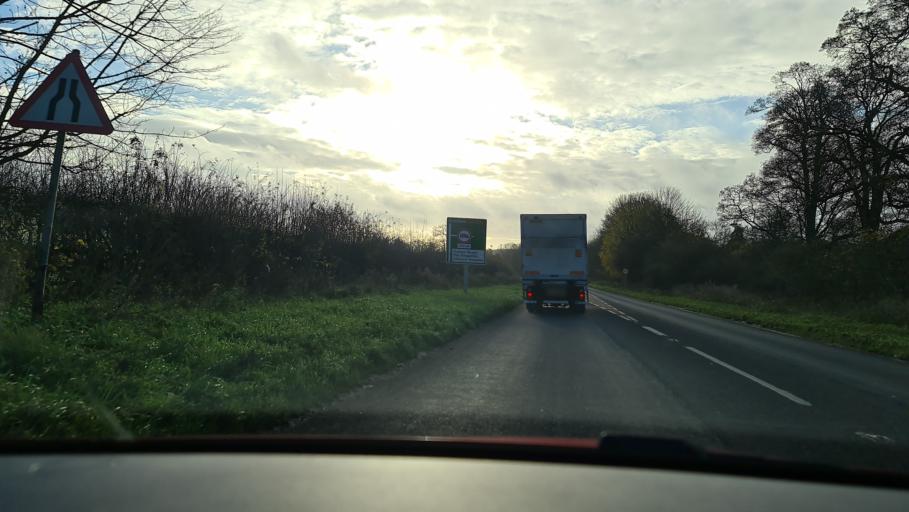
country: GB
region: England
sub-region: Buckinghamshire
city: Great Missenden
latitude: 51.6926
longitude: -0.6939
